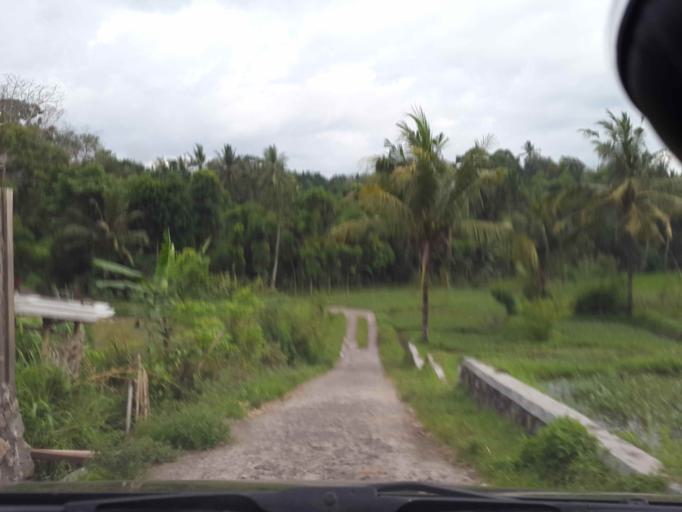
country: ID
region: West Nusa Tenggara
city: Jejelok
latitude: -8.6128
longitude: 116.1767
